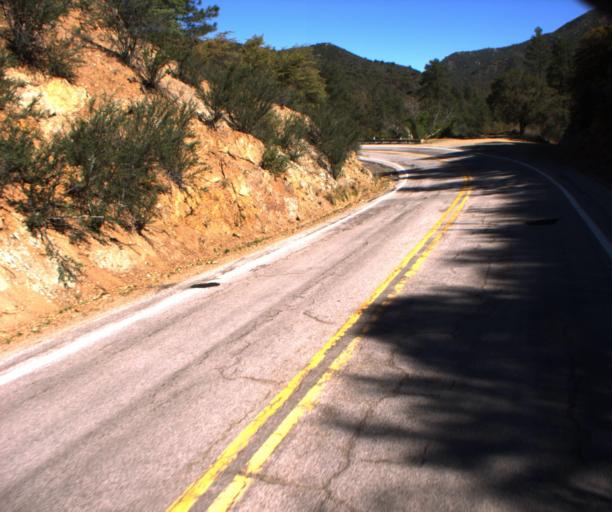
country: US
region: Arizona
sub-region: Yavapai County
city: Prescott
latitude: 34.4541
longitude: -112.5365
